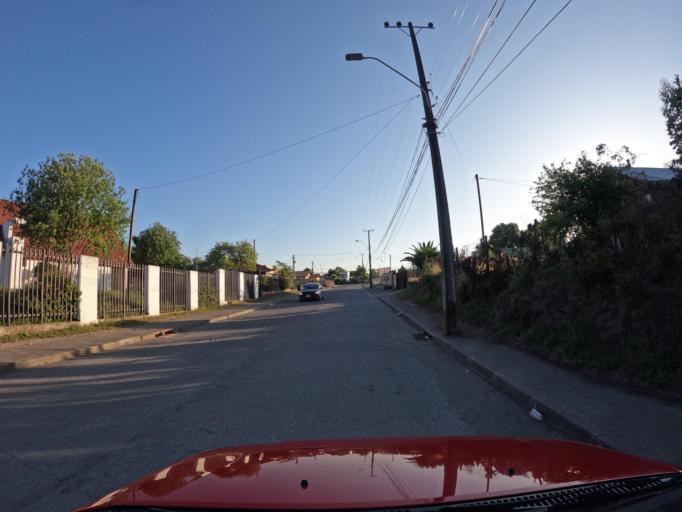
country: CL
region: Biobio
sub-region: Provincia de Concepcion
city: Lota
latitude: -37.1683
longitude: -72.9469
